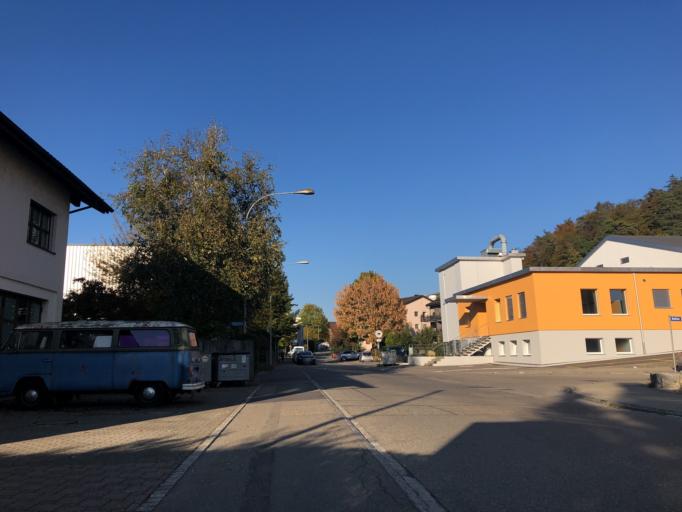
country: CH
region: Zurich
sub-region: Bezirk Pfaeffikon
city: Effretikon
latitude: 47.4209
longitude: 8.6834
